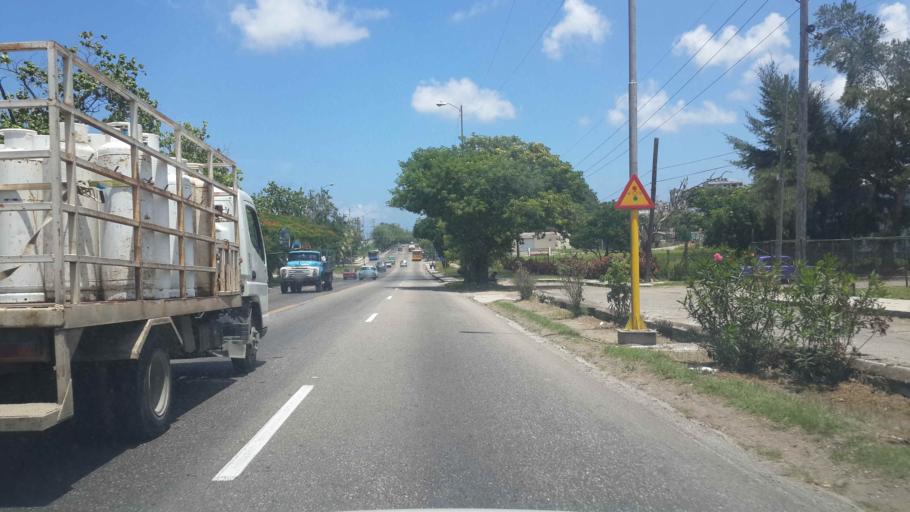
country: CU
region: La Habana
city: Guanabacoa
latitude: 23.1301
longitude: -82.3142
